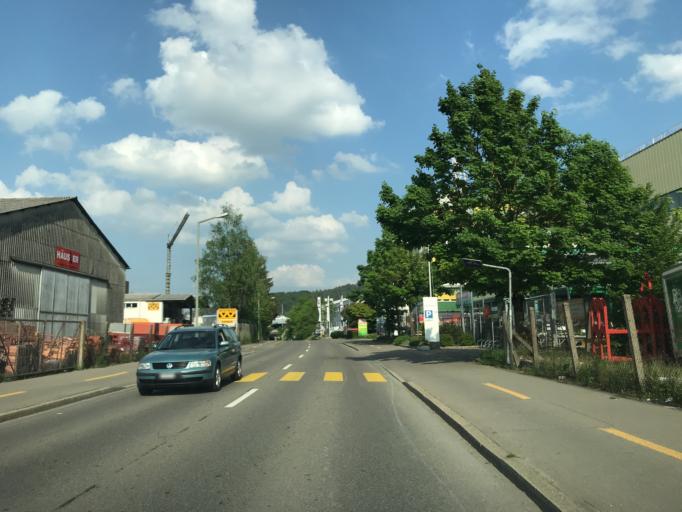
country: CH
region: Zurich
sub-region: Bezirk Winterthur
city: Mattenbach (Kreis 7) / Gutschick
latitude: 47.4965
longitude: 8.7541
